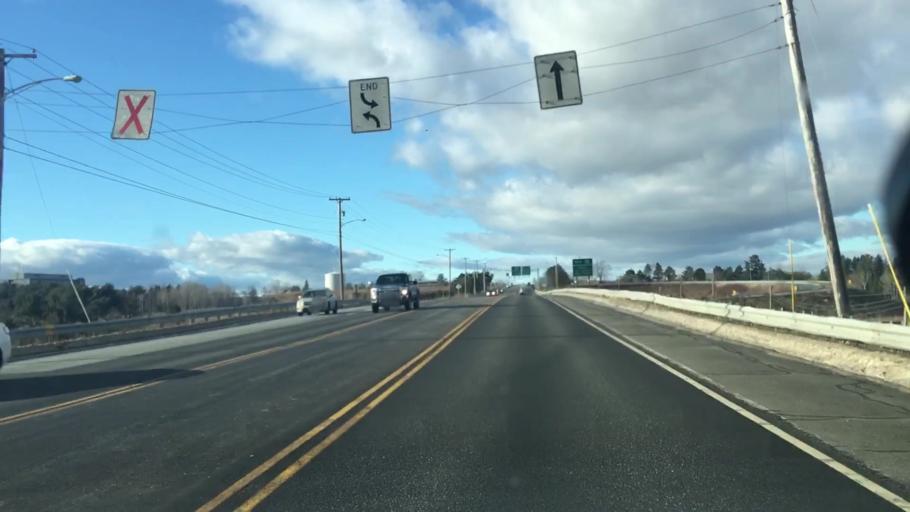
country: US
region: Maine
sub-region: Penobscot County
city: Holden
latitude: 44.7697
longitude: -68.7176
